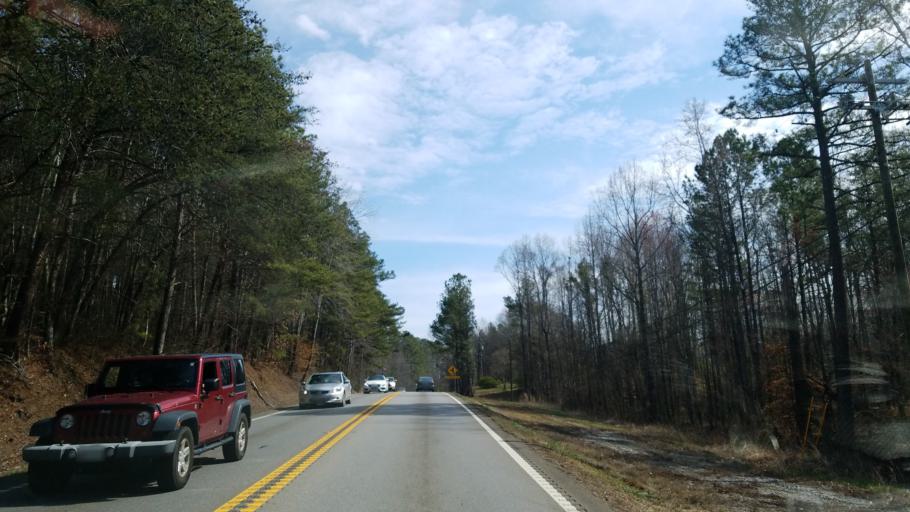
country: US
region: Georgia
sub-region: Cherokee County
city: Canton
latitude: 34.2165
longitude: -84.4592
